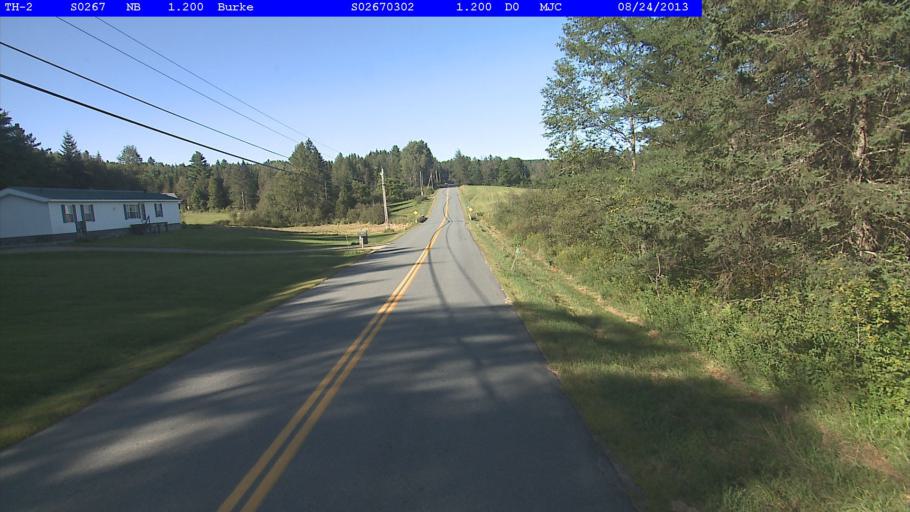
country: US
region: Vermont
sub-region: Caledonia County
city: Lyndonville
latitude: 44.6036
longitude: -71.9392
